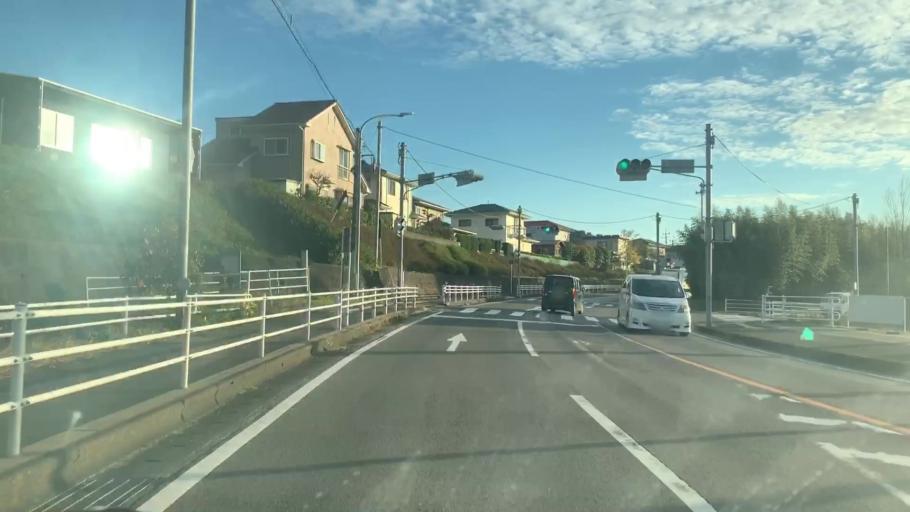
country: JP
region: Saga Prefecture
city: Karatsu
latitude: 33.3986
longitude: 129.9877
